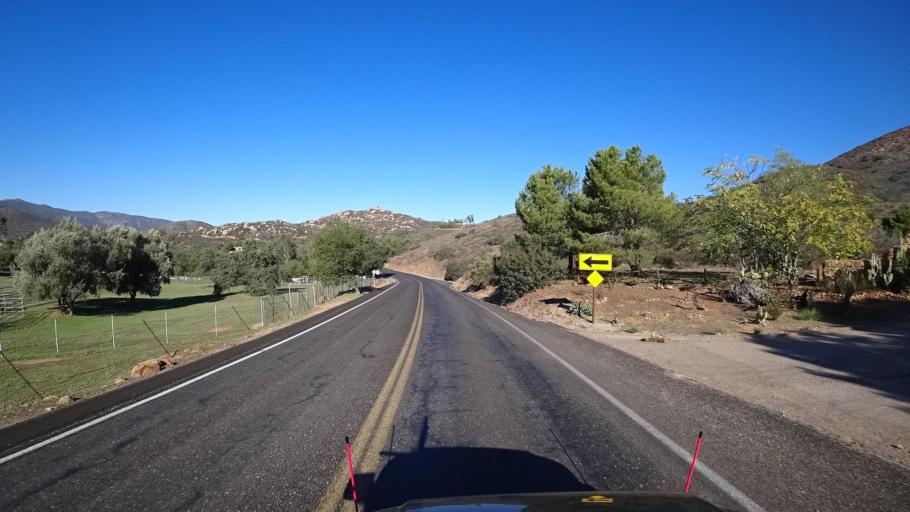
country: MX
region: Baja California
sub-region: Tijuana
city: Villa del Campo
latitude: 32.6230
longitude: -116.7486
